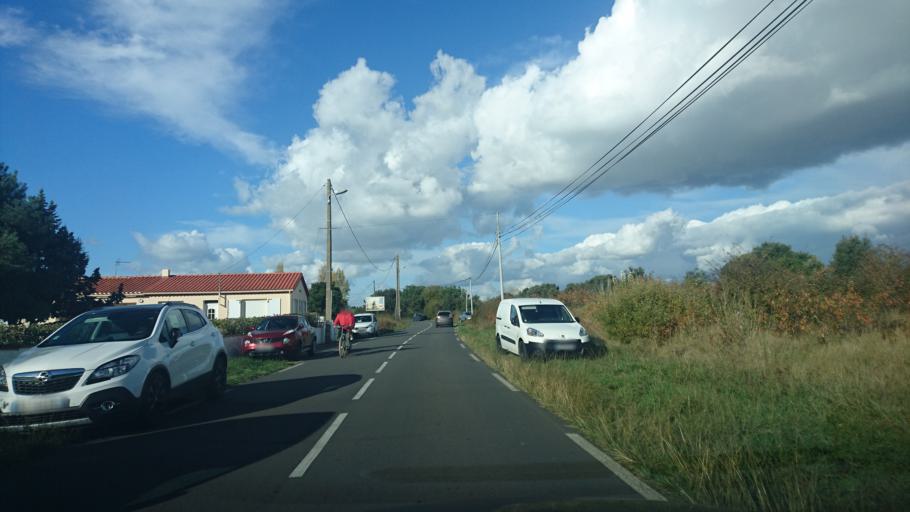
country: FR
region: Pays de la Loire
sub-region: Departement de la Vendee
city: Les Sables-d'Olonne
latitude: 46.5124
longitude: -1.8040
